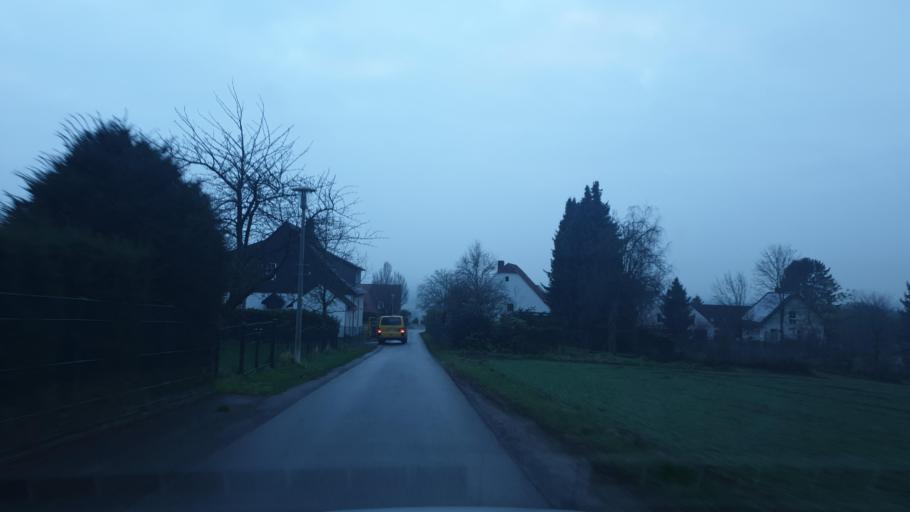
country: DE
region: North Rhine-Westphalia
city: Bad Oeynhausen
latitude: 52.2452
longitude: 8.8410
